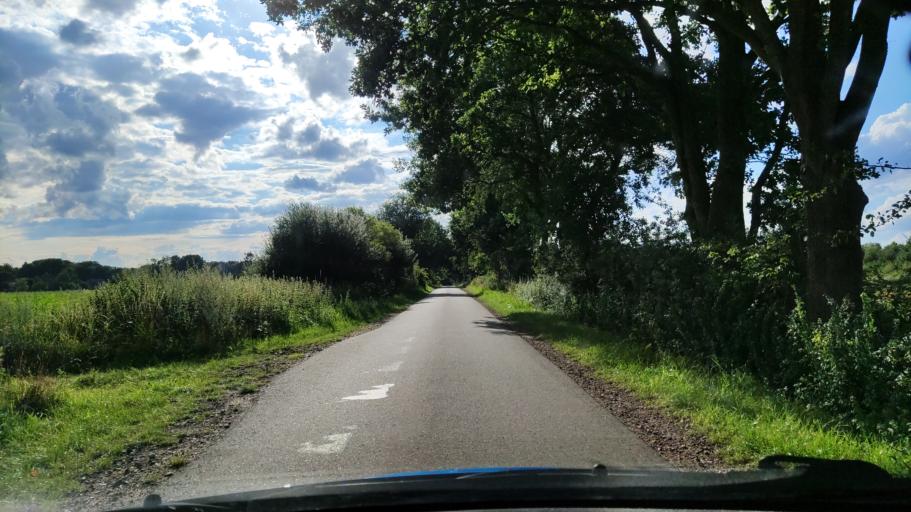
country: DE
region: Lower Saxony
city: Nahrendorf
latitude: 53.1795
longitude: 10.7904
